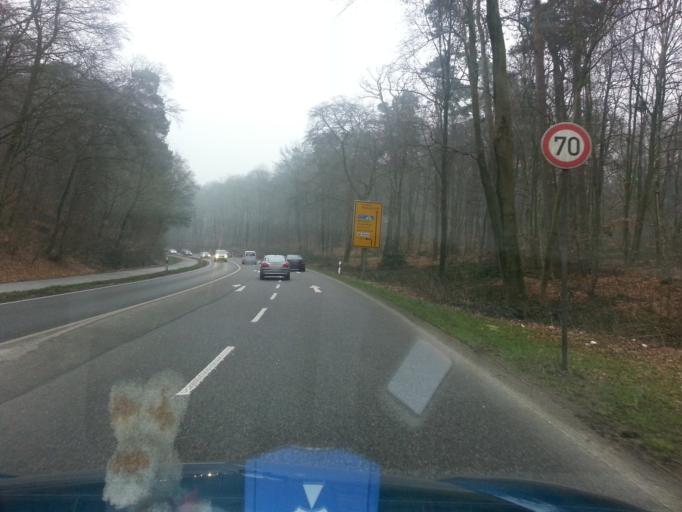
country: DE
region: North Rhine-Westphalia
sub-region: Regierungsbezirk Dusseldorf
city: Kleve
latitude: 51.7720
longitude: 6.1439
